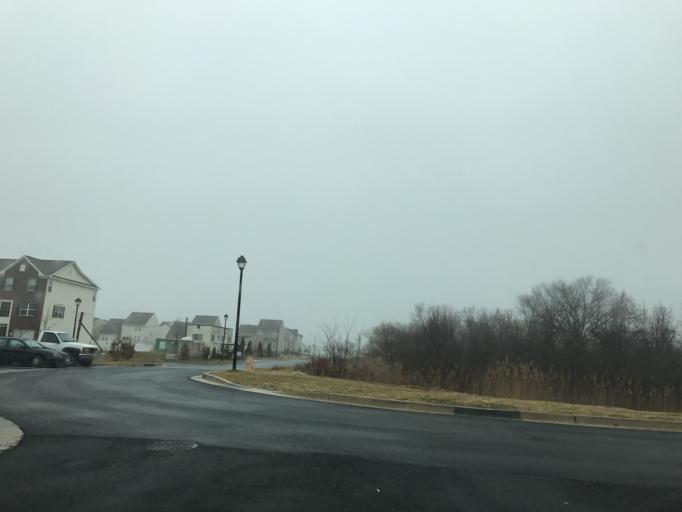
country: US
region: Maryland
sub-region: Baltimore County
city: Dundalk
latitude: 39.2503
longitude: -76.4938
